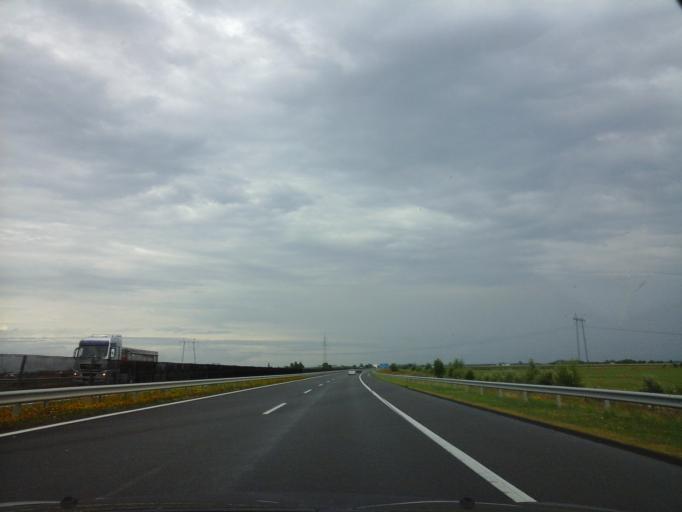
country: HU
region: Hajdu-Bihar
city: Polgar
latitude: 47.8280
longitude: 21.1508
